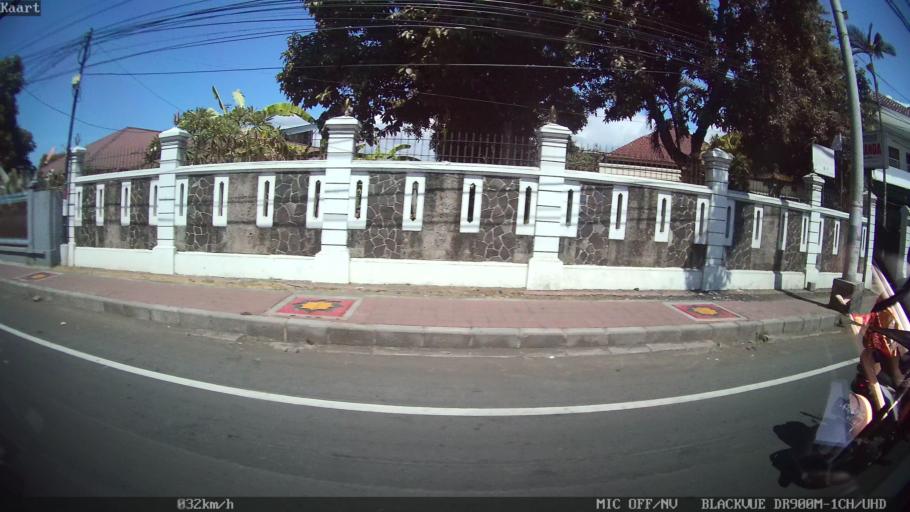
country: ID
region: Bali
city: Banjar Kaliuntu Satu
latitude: -8.1189
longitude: 115.0745
